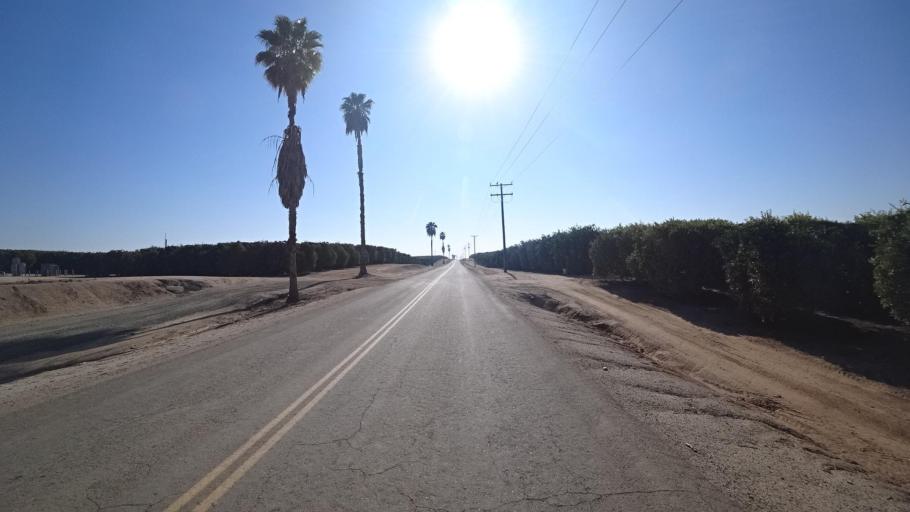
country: US
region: California
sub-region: Tulare County
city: Richgrove
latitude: 35.7148
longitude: -119.1339
